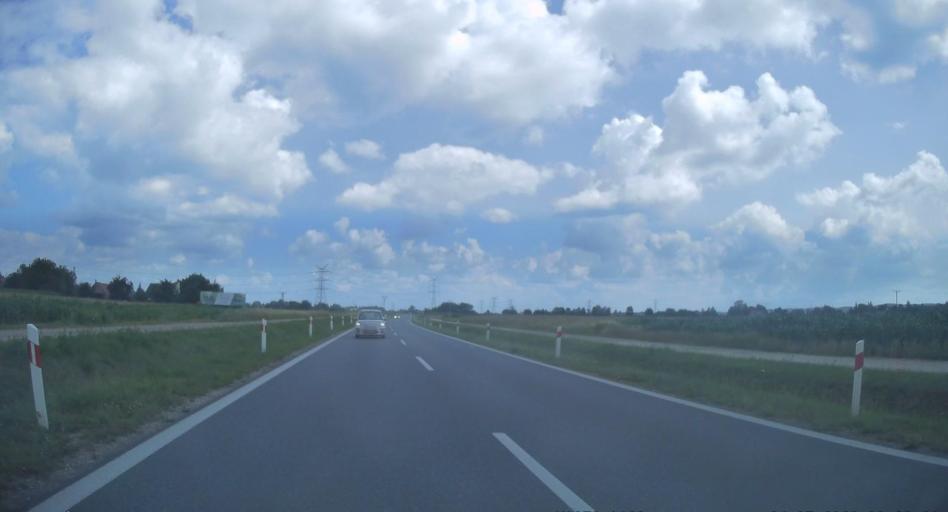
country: PL
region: Lesser Poland Voivodeship
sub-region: Powiat tarnowski
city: Wojnicz
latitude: 49.9403
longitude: 20.8449
